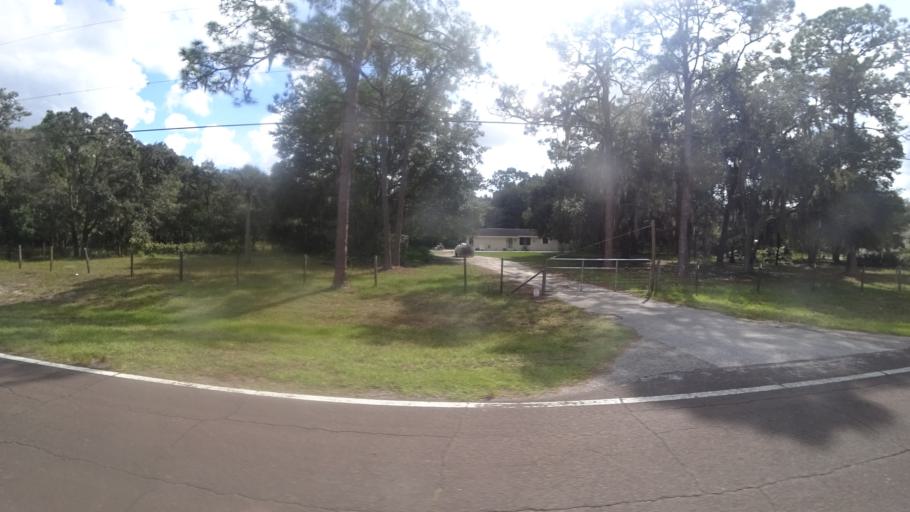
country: US
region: Florida
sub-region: Hillsborough County
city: Ruskin
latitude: 27.6485
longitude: -82.4004
